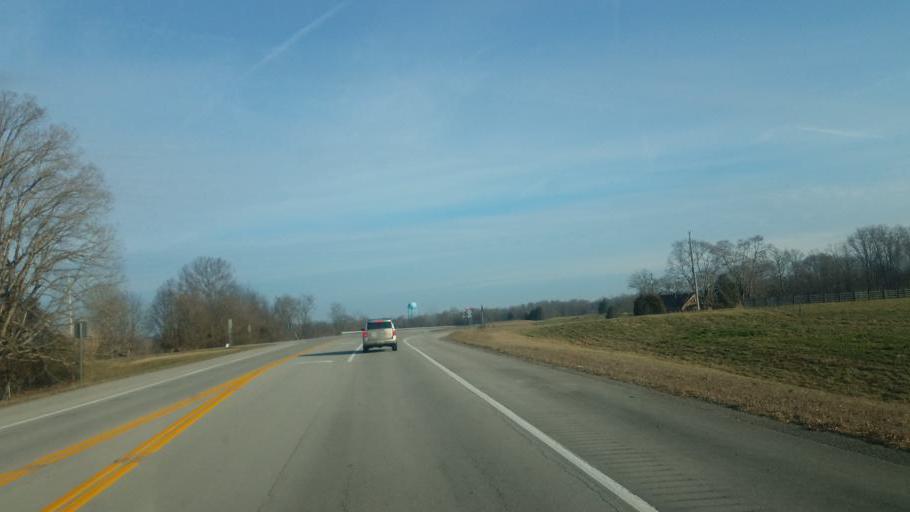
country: US
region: Kentucky
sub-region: Russell County
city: Jamestown
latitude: 36.9910
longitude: -85.0835
